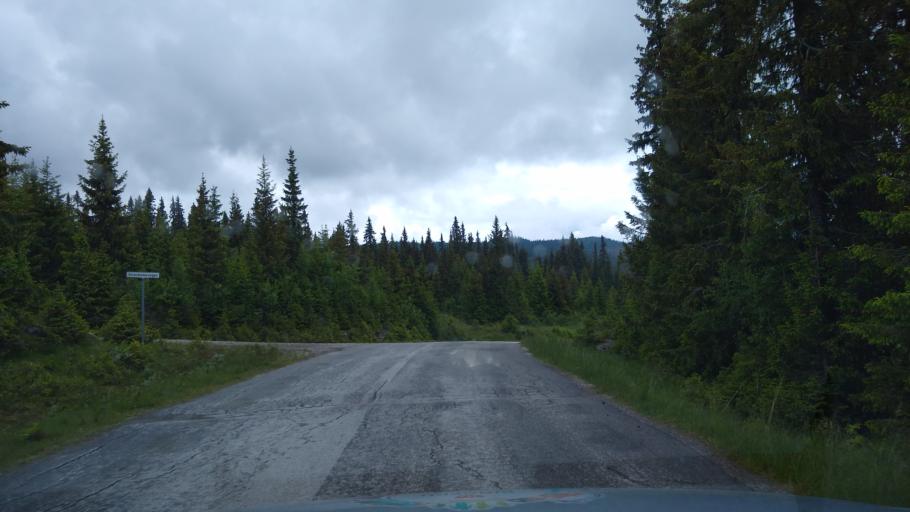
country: NO
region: Oppland
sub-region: Ringebu
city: Ringebu
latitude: 61.4887
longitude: 10.1129
